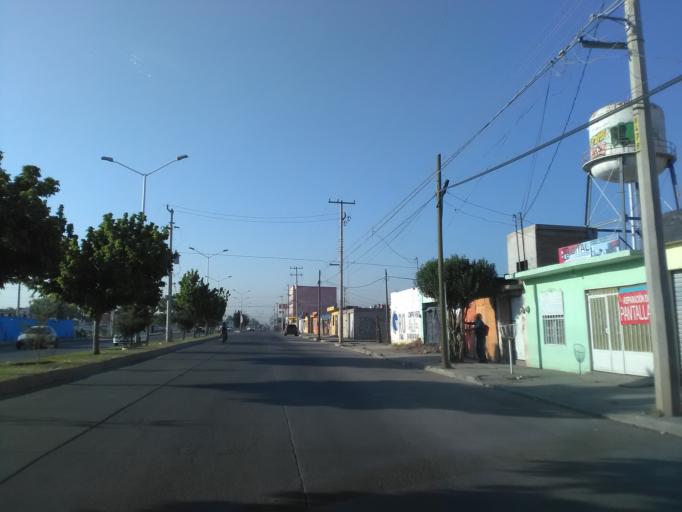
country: MX
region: Durango
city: Victoria de Durango
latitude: 24.0584
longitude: -104.6304
